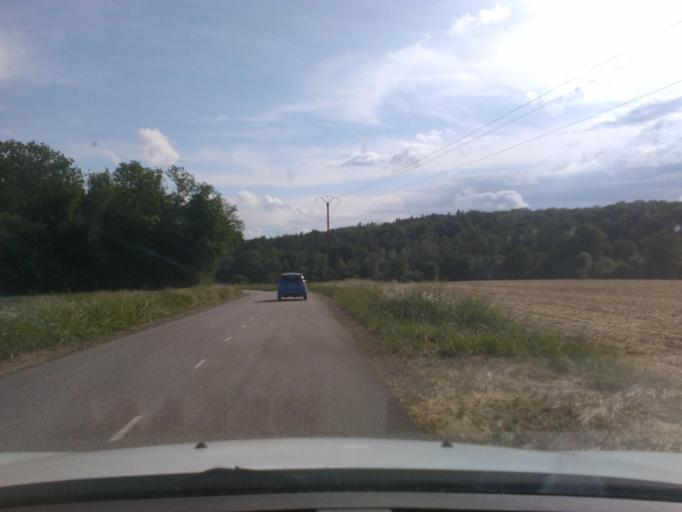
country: FR
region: Lorraine
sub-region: Departement de Meurthe-et-Moselle
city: Baccarat
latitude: 48.5057
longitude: 6.7109
